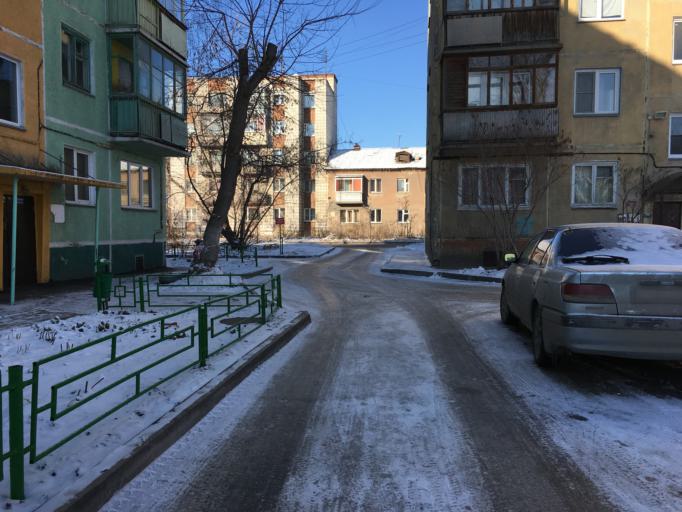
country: RU
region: Novosibirsk
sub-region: Novosibirskiy Rayon
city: Novosibirsk
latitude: 55.0552
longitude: 82.9681
